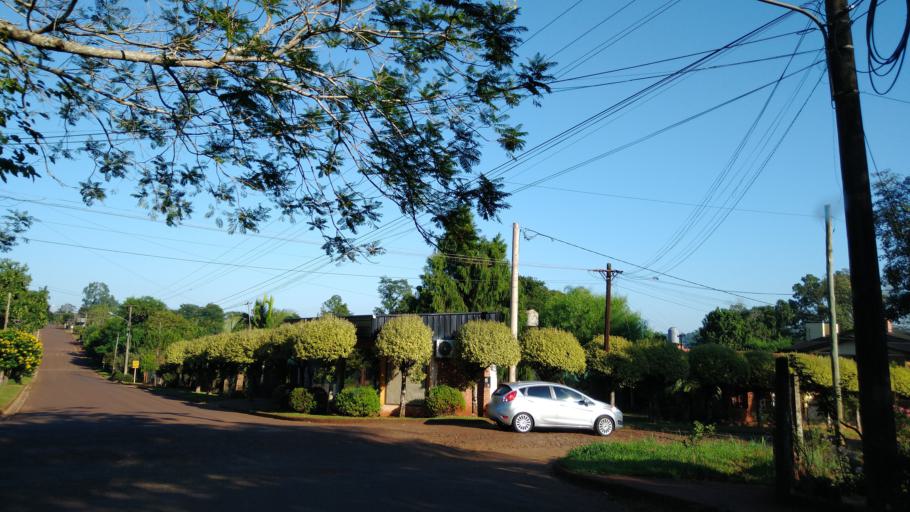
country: AR
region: Misiones
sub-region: Departamento de Montecarlo
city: Montecarlo
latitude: -26.5650
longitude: -54.7520
